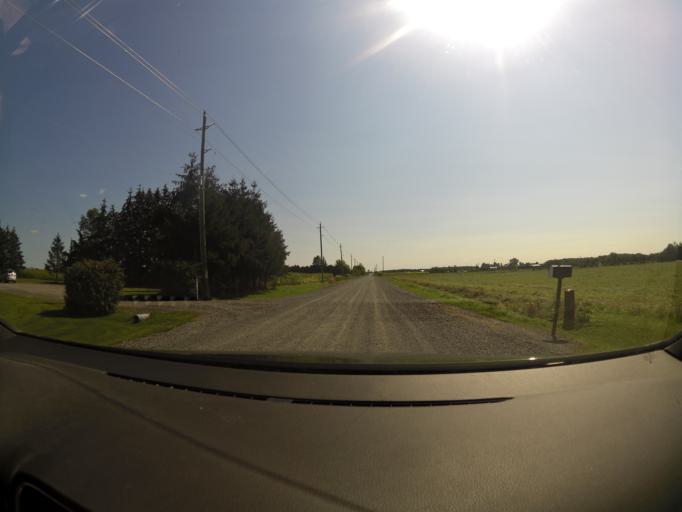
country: CA
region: Ontario
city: Arnprior
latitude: 45.3249
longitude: -76.2654
